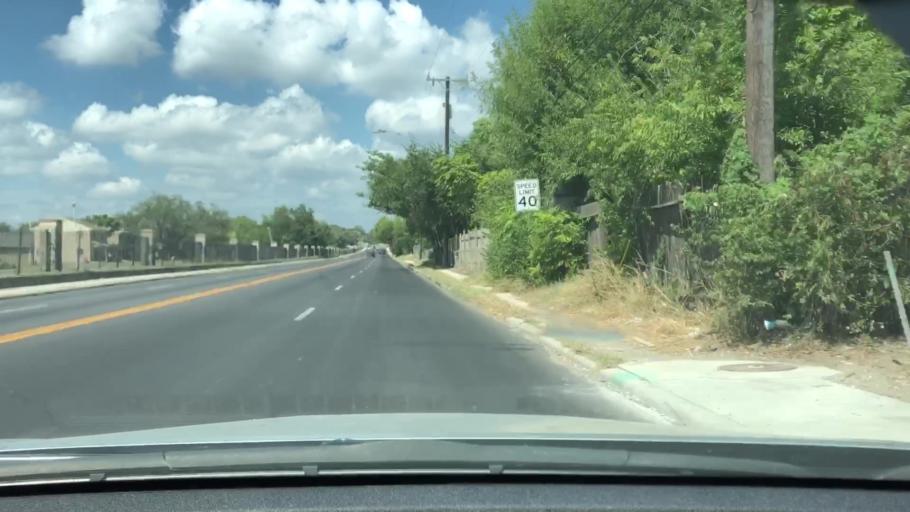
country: US
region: Texas
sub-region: Bexar County
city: Terrell Hills
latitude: 29.4849
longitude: -98.4231
